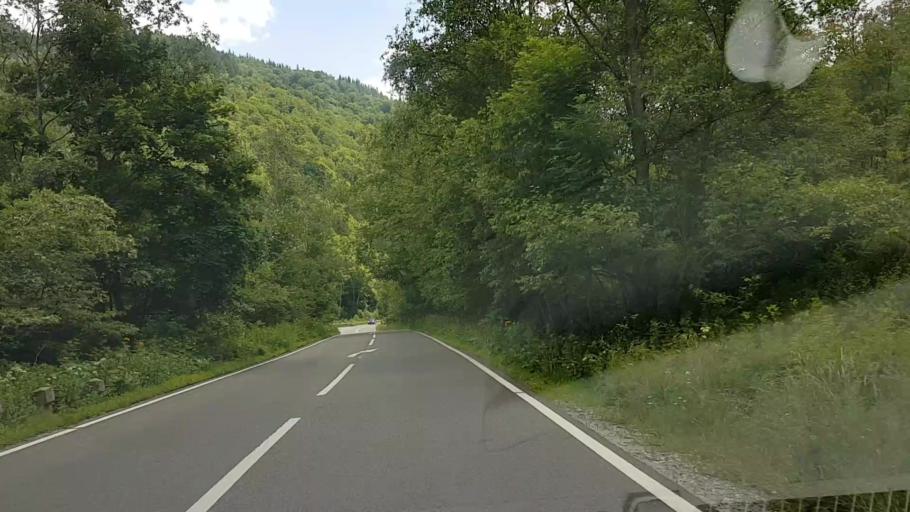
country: RO
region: Suceava
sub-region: Comuna Crucea
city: Crucea
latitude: 47.3233
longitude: 25.6246
